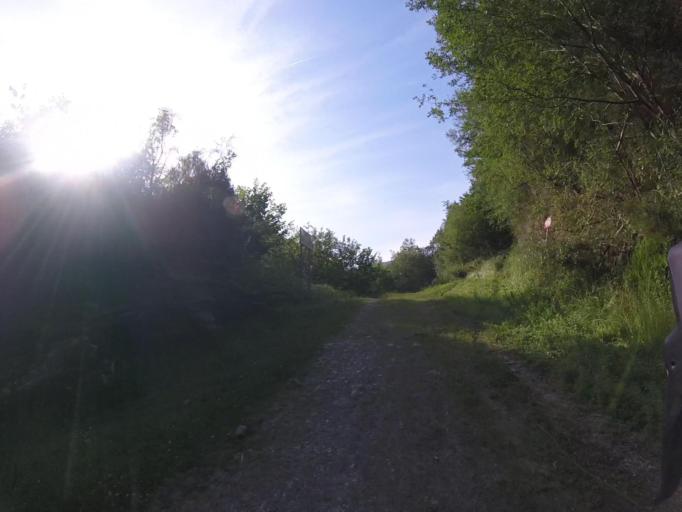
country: ES
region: Navarre
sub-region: Provincia de Navarra
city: Arano
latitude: 43.2361
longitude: -1.8697
